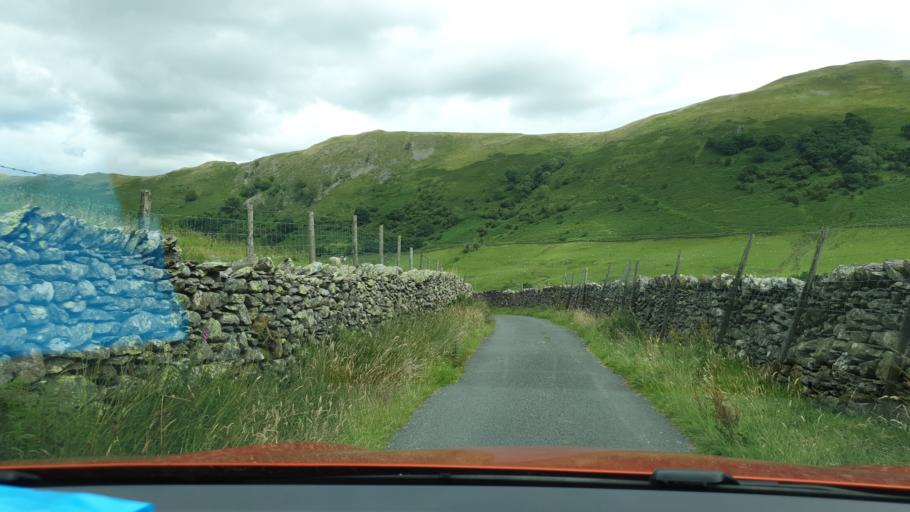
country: GB
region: England
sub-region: Cumbria
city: Ambleside
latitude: 54.5416
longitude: -2.8763
